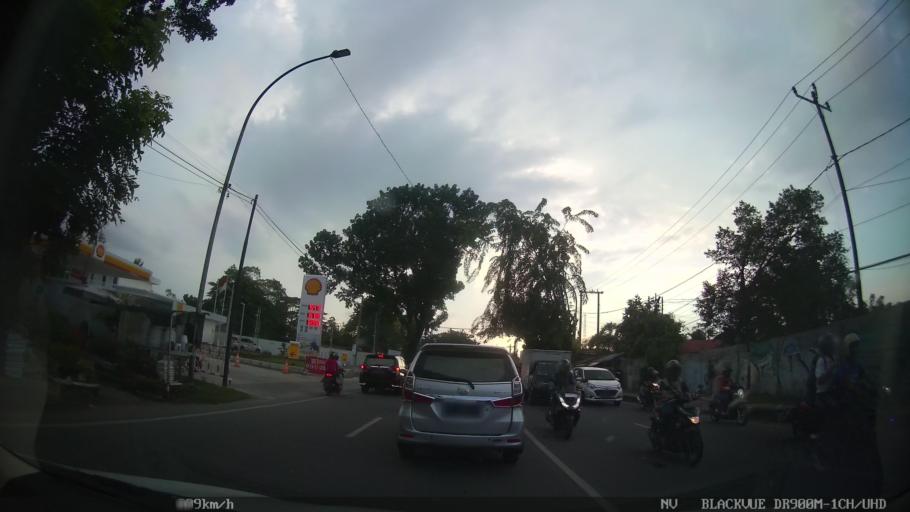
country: ID
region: North Sumatra
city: Medan
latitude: 3.6061
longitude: 98.6722
